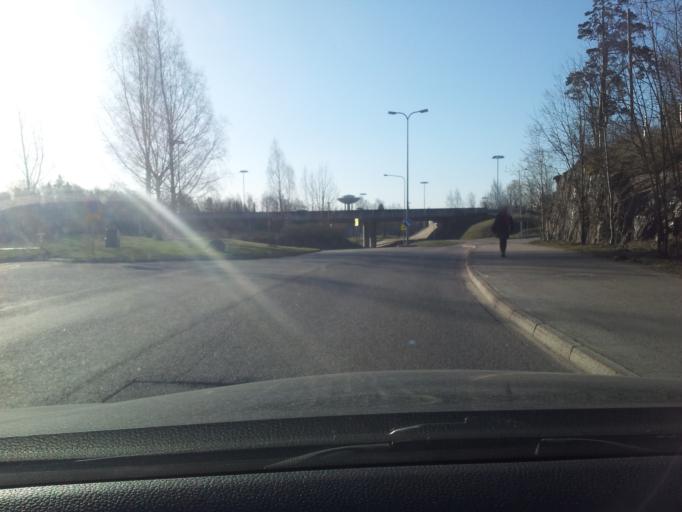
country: FI
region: Uusimaa
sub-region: Helsinki
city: Koukkuniemi
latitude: 60.1684
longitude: 24.7498
